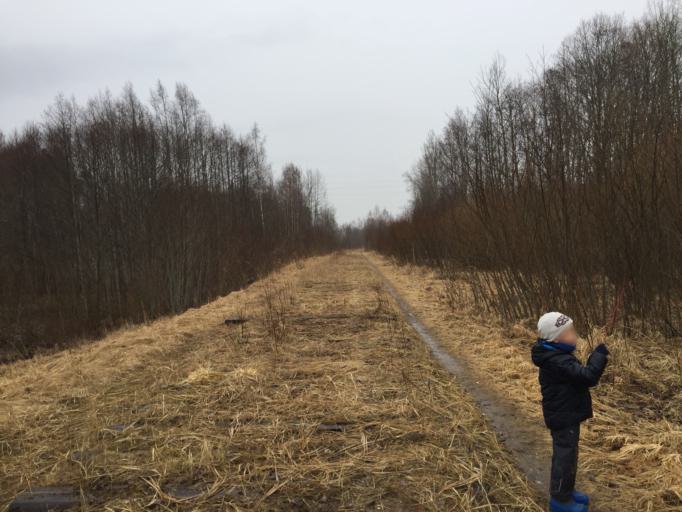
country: LV
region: Lielvarde
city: Lielvarde
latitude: 56.7293
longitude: 24.7777
